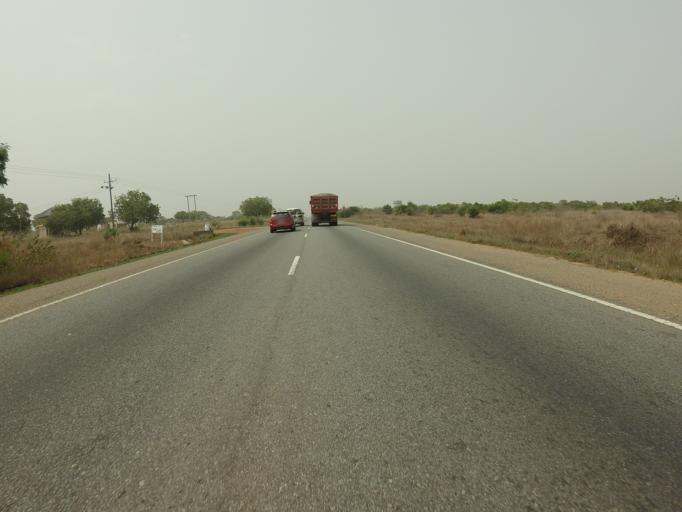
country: GH
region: Greater Accra
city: Tema
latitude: 5.8701
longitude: 0.3226
